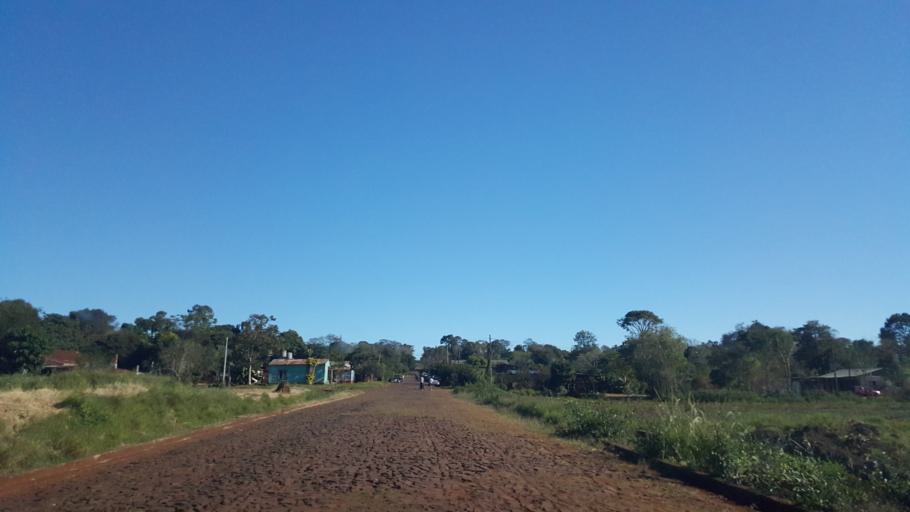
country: AR
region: Misiones
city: Gobernador Roca
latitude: -27.1861
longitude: -55.4658
